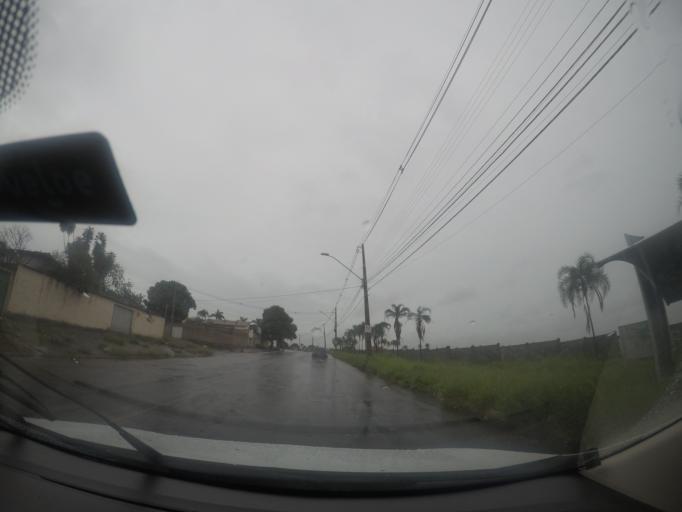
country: BR
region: Goias
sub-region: Goiania
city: Goiania
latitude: -16.6587
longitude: -49.3163
